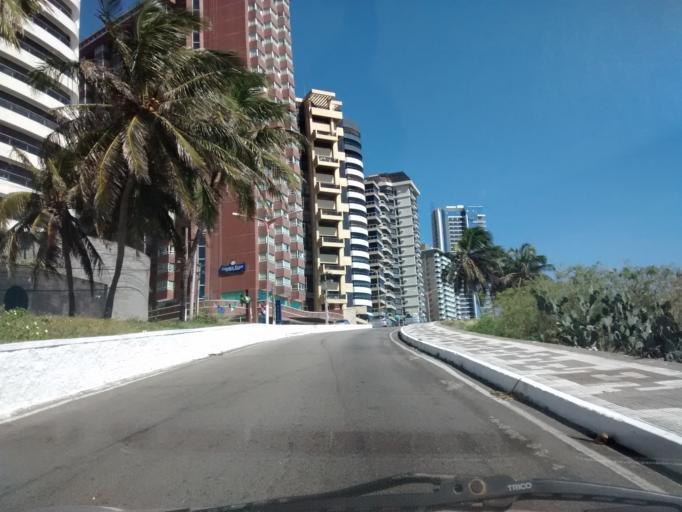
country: BR
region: Rio Grande do Norte
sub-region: Natal
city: Natal
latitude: -5.7837
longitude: -35.1930
